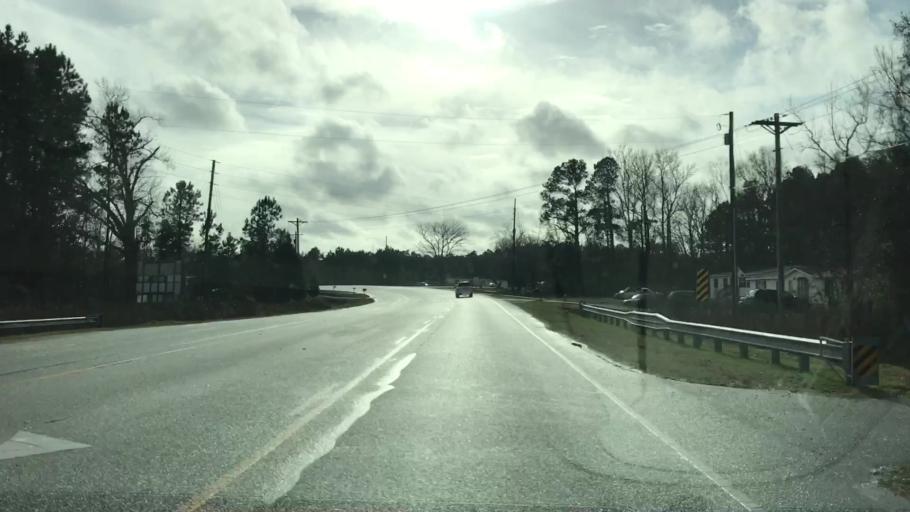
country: US
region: South Carolina
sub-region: Williamsburg County
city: Andrews
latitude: 33.4439
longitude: -79.5898
